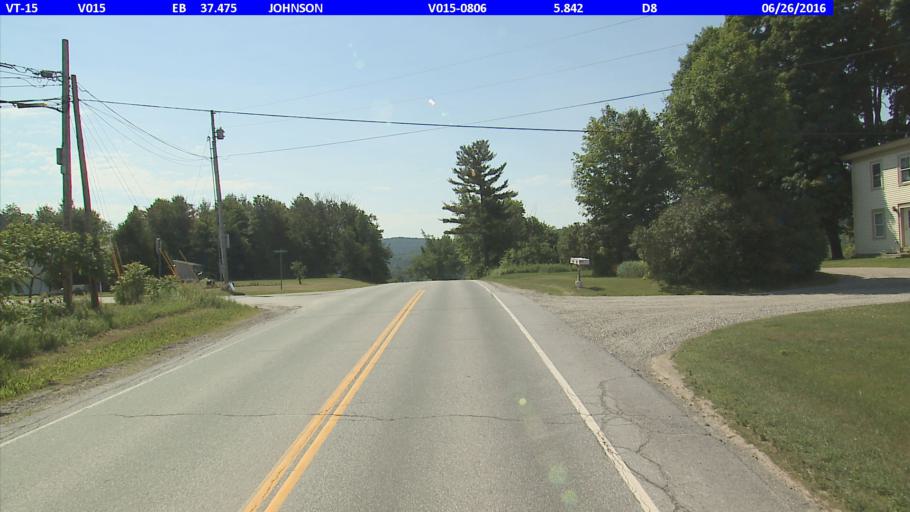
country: US
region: Vermont
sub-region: Lamoille County
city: Johnson
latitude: 44.6176
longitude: -72.6627
